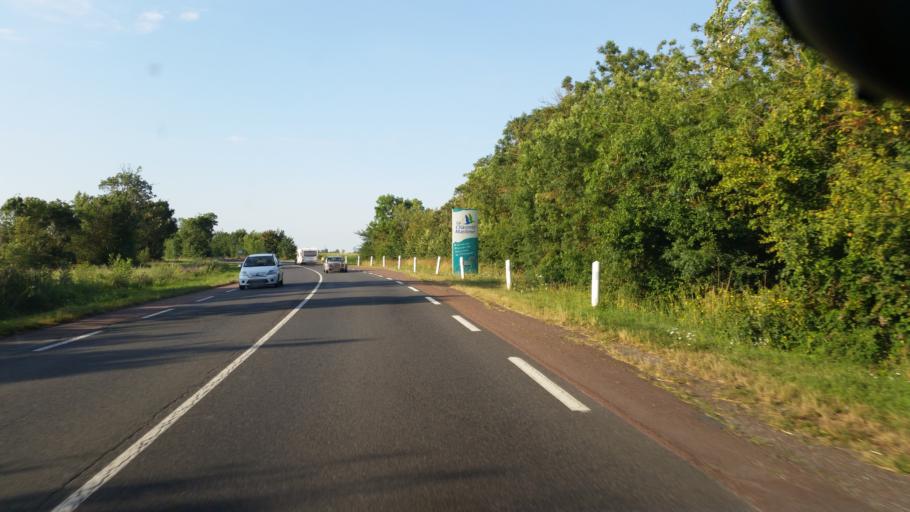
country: FR
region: Poitou-Charentes
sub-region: Departement de la Charente-Maritime
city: Marans
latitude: 46.3418
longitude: -0.9990
